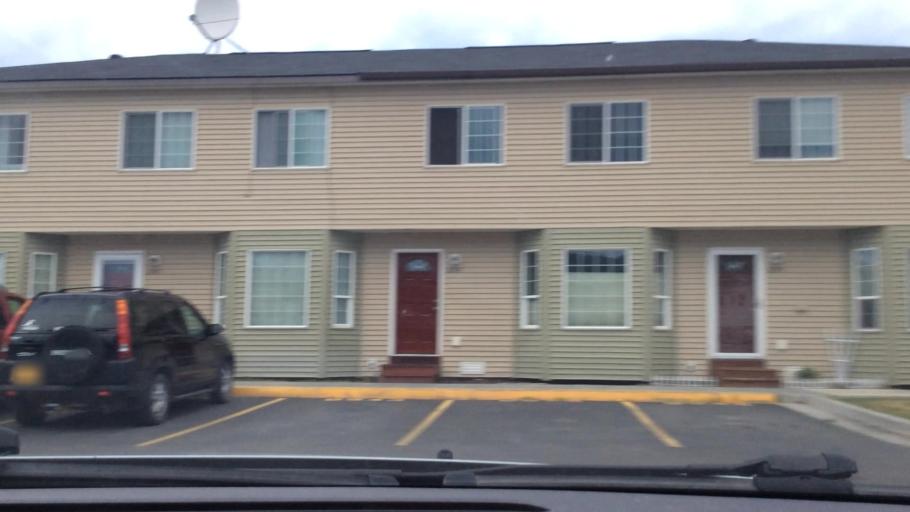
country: US
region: Alaska
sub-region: Anchorage Municipality
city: Elmendorf Air Force Base
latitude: 61.2228
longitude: -149.7584
